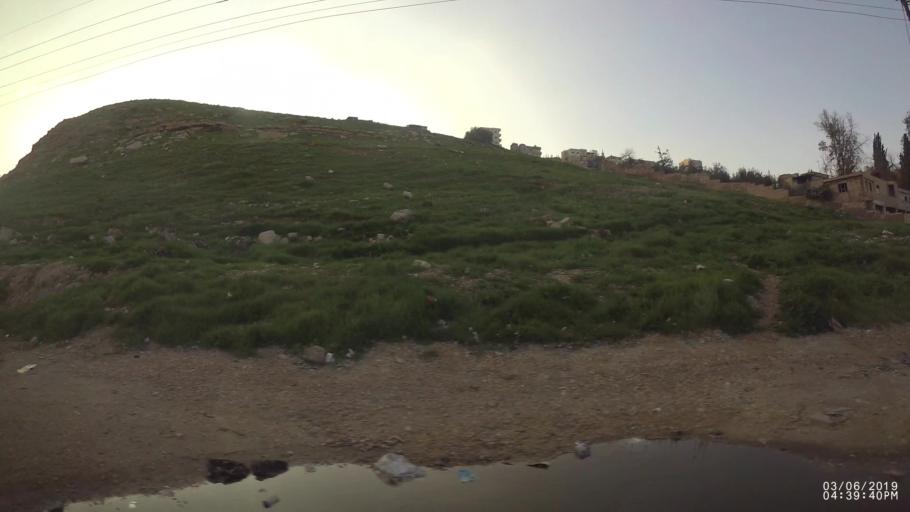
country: JO
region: Amman
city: Amman
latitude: 31.9833
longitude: 35.9757
